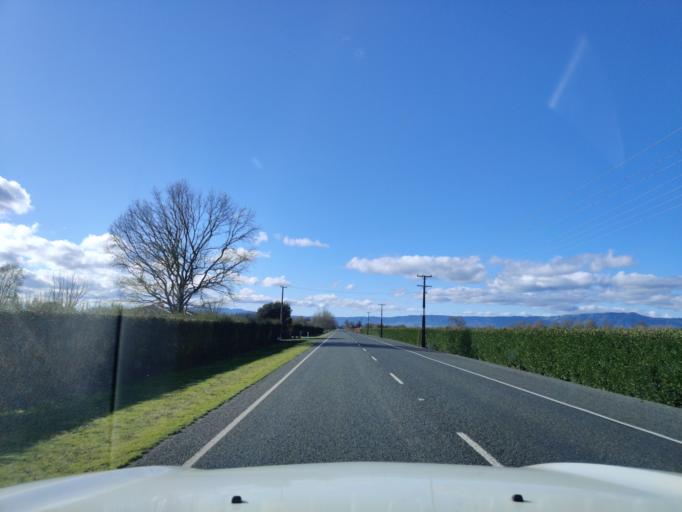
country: NZ
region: Waikato
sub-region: Matamata-Piako District
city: Matamata
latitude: -37.8741
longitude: 175.7426
